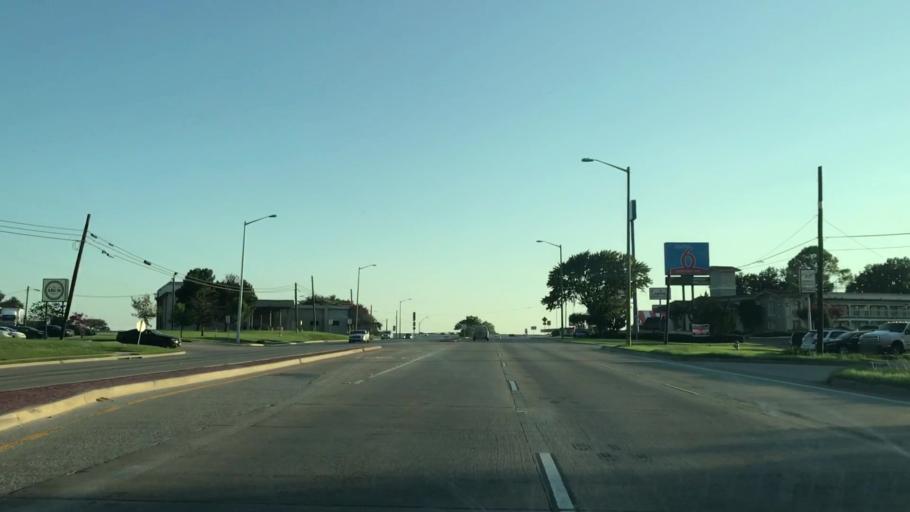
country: US
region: Texas
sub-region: Denton County
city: Denton
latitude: 33.1994
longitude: -97.1378
